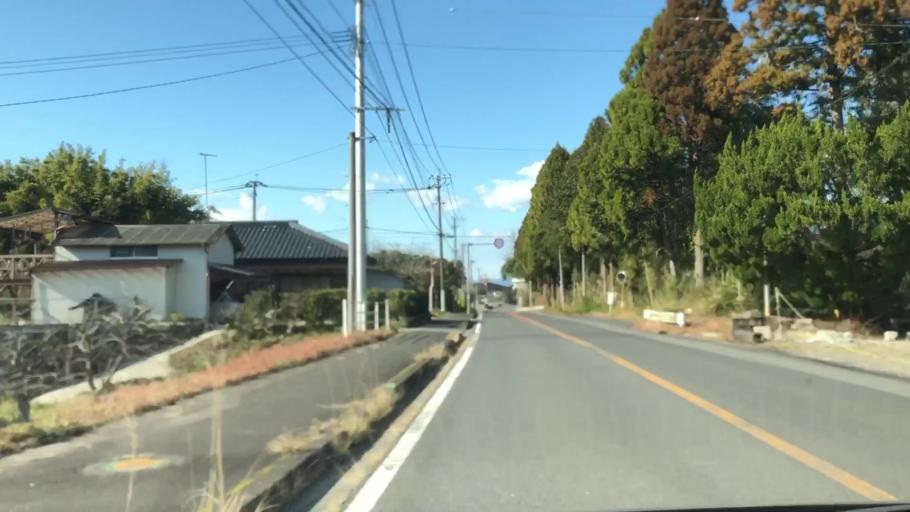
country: JP
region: Kagoshima
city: Satsumasendai
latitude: 31.7987
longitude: 130.4393
